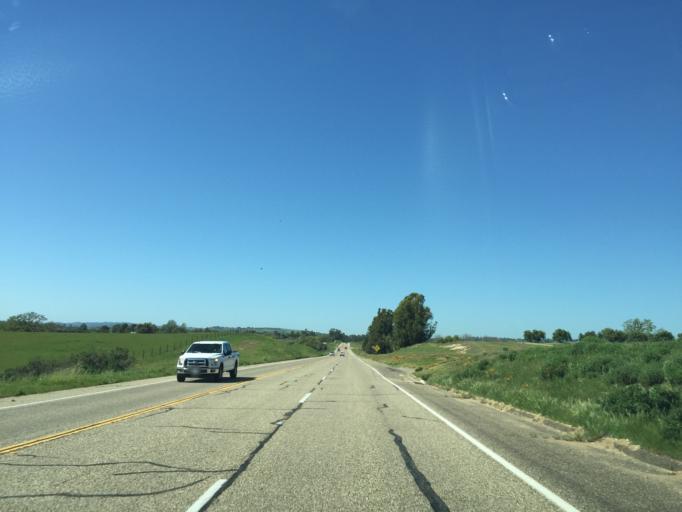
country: US
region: California
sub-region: Santa Barbara County
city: Santa Ynez
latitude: 34.6204
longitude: -120.0667
